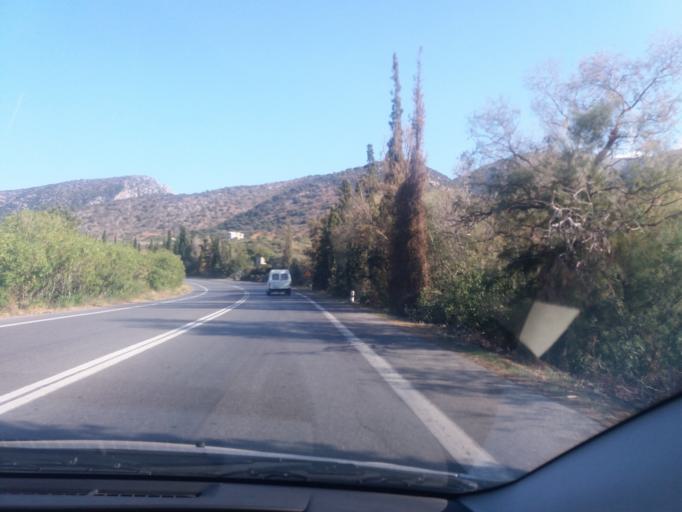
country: GR
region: Crete
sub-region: Nomos Lasithiou
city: Sision
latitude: 35.2924
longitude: 25.5204
